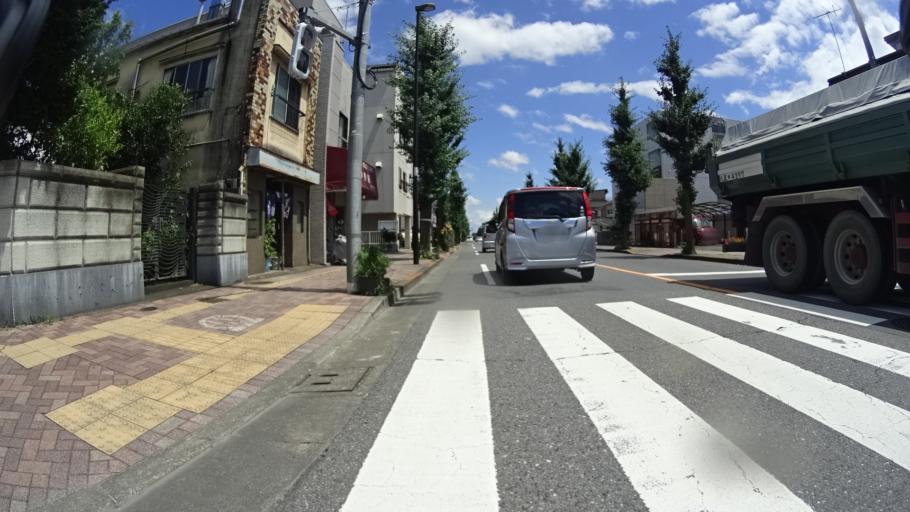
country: JP
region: Tokyo
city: Ome
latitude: 35.7839
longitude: 139.2822
